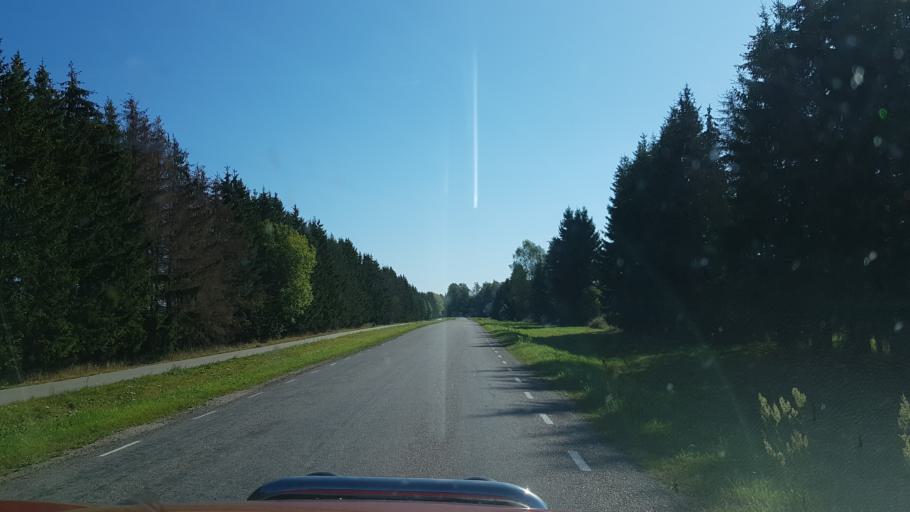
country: EE
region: Tartu
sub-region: Tartu linn
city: Tartu
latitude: 58.3574
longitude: 26.8632
